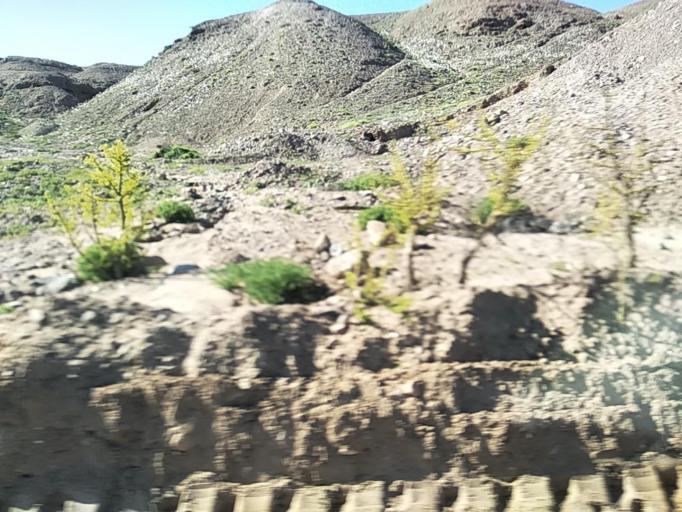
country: CL
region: Atacama
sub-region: Provincia de Copiapo
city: Copiapo
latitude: -27.3356
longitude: -70.7739
